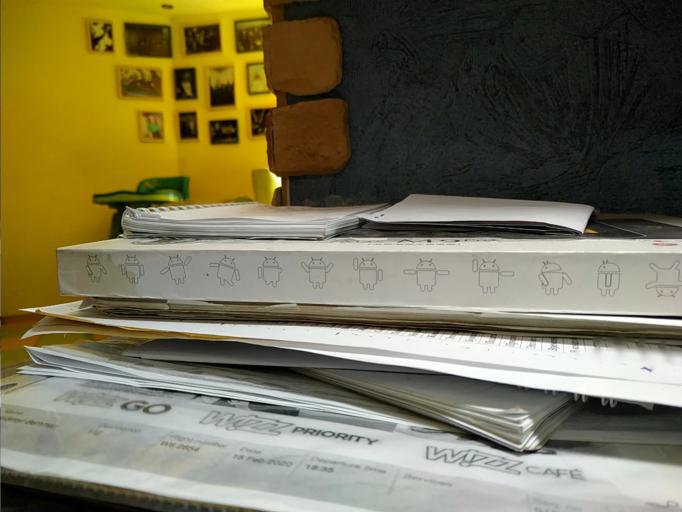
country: RU
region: Novgorod
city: Utorgosh
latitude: 58.2624
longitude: 29.8847
